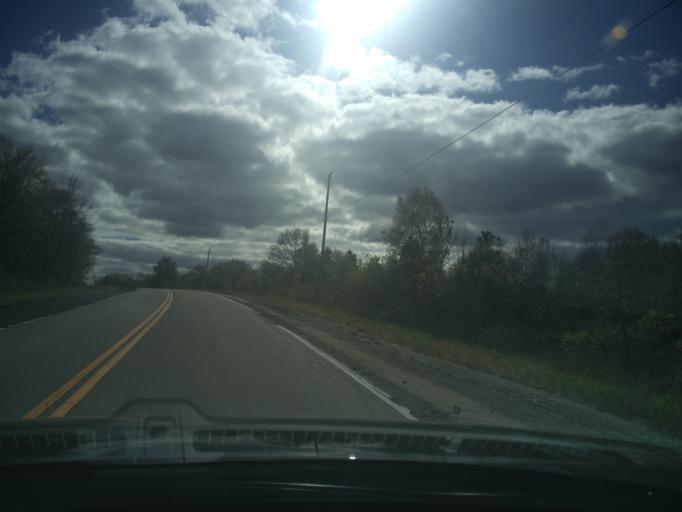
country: CA
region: Ontario
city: Perth
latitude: 44.7531
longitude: -76.3901
